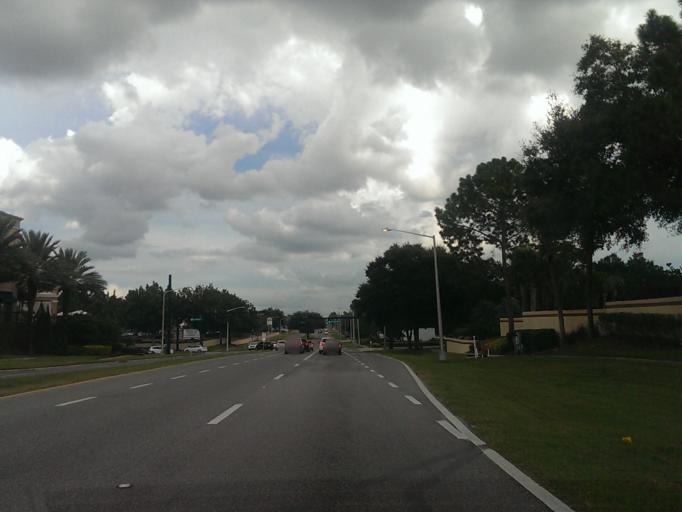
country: US
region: Florida
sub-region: Orange County
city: Doctor Phillips
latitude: 28.4499
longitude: -81.4928
